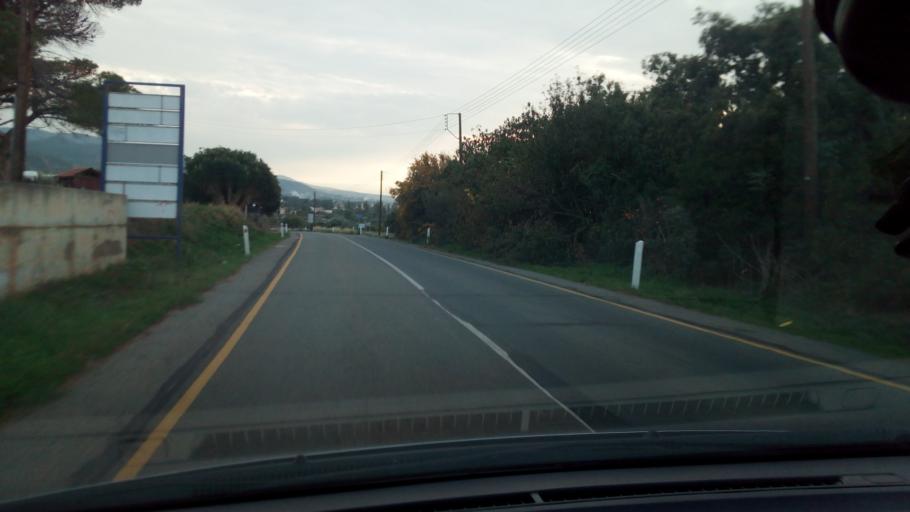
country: CY
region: Pafos
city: Polis
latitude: 35.1355
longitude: 32.5207
